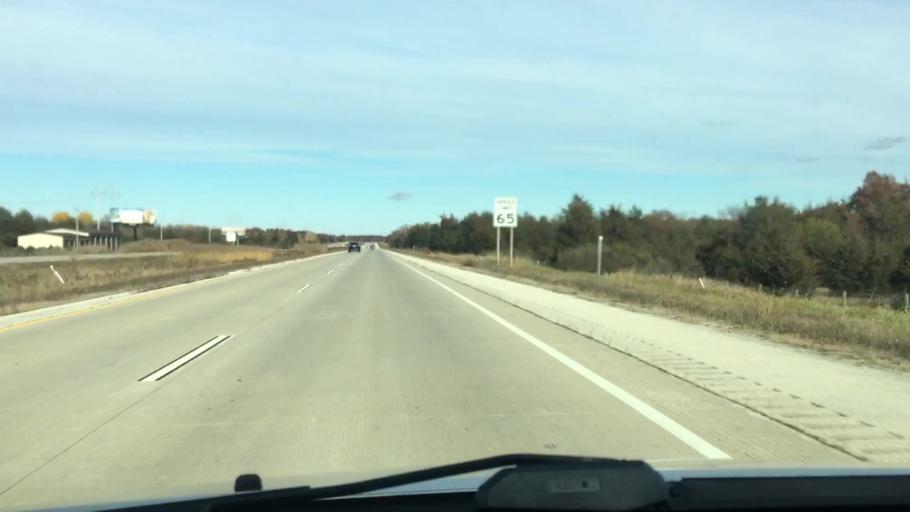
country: US
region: Wisconsin
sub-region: Kewaunee County
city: Luxemburg
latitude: 44.6212
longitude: -87.8228
